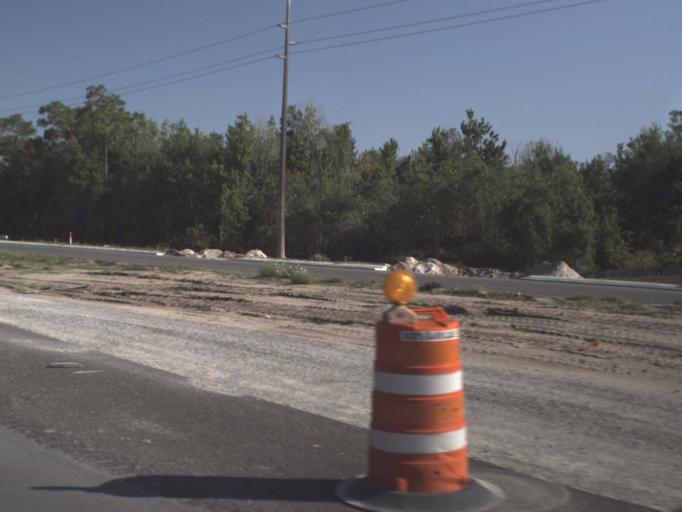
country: US
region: Florida
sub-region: Lake County
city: Four Corners
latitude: 28.4284
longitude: -81.7118
